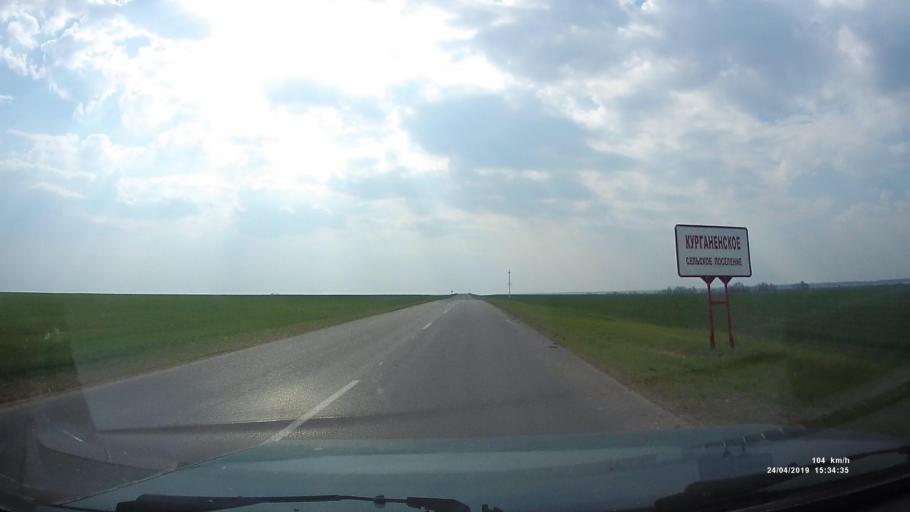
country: RU
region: Kalmykiya
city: Yashalta
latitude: 46.5992
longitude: 42.9133
